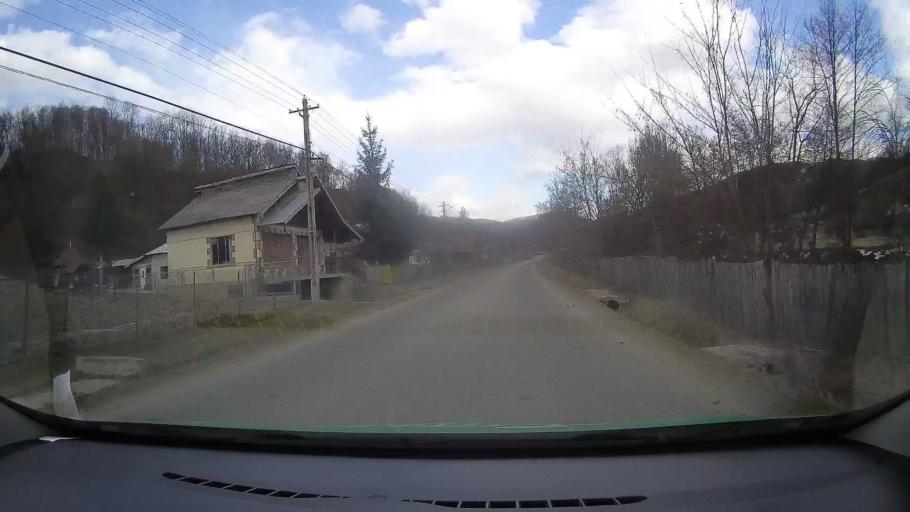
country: RO
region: Dambovita
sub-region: Comuna Visinesti
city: Visinesti
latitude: 45.0683
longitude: 25.5465
